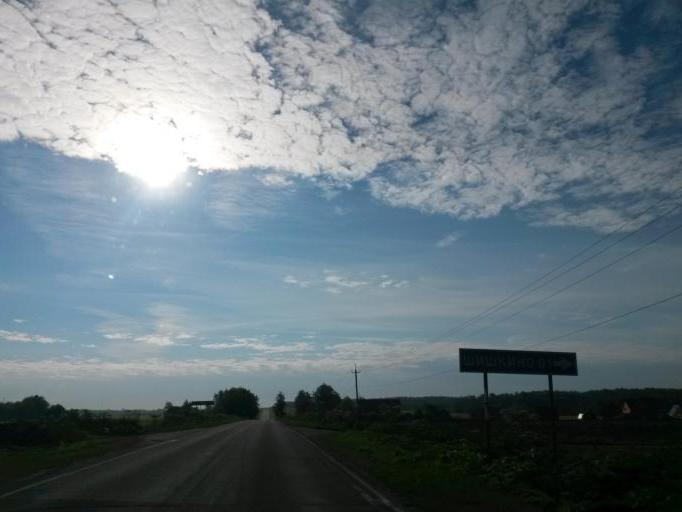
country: RU
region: Moskovskaya
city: Belyye Stolby
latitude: 55.2682
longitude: 37.7765
